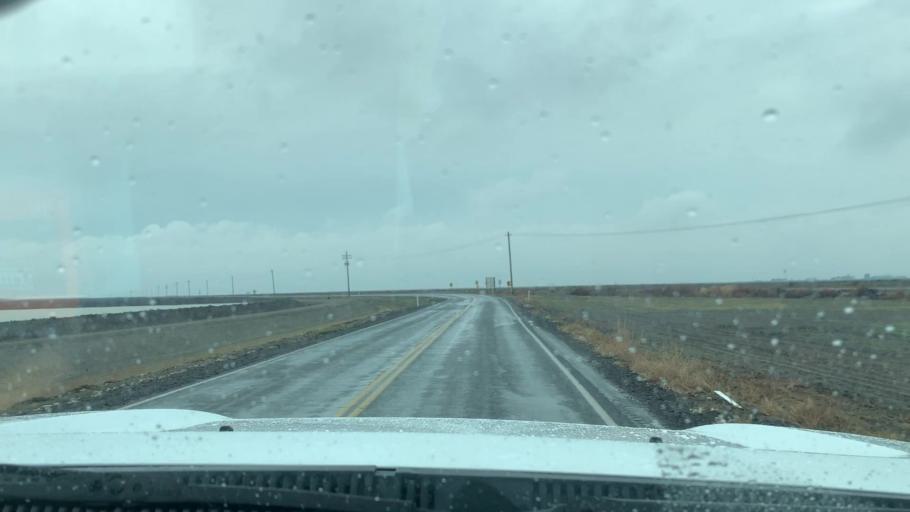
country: US
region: California
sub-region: Tulare County
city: Alpaugh
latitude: 35.9621
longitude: -119.5724
